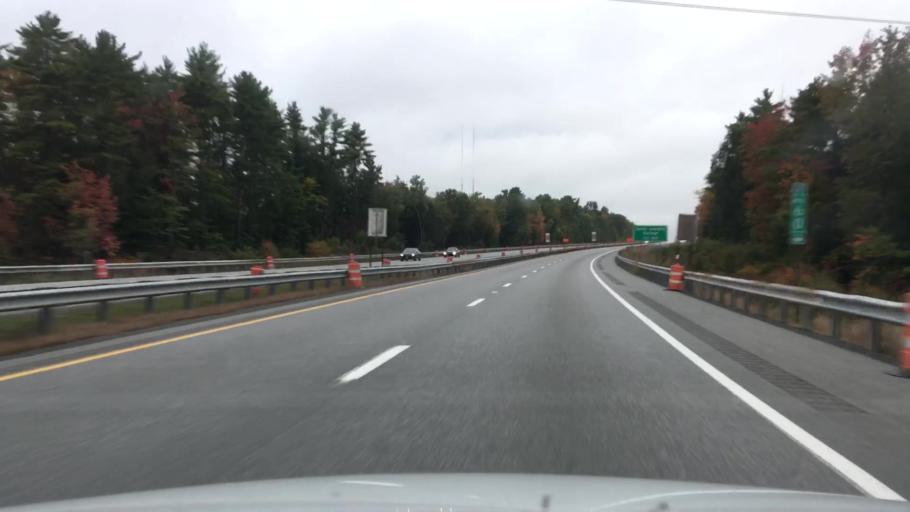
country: US
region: Maine
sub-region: Cumberland County
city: Cumberland Center
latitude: 43.8385
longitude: -70.3246
